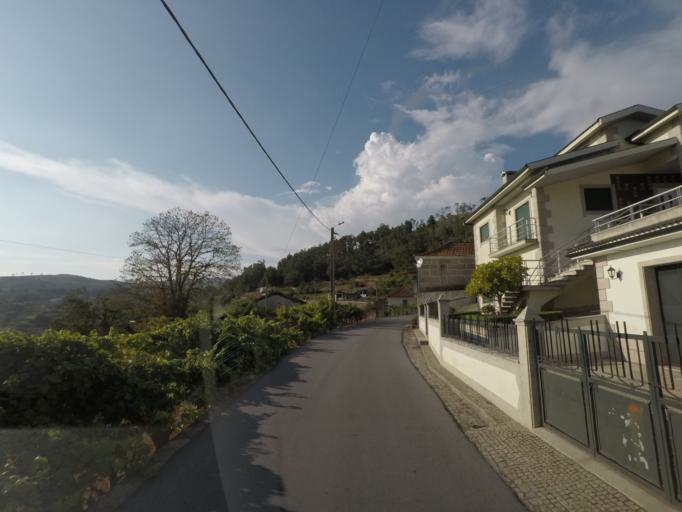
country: PT
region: Vila Real
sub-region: Mesao Frio
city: Mesao Frio
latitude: 41.1642
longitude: -7.9206
